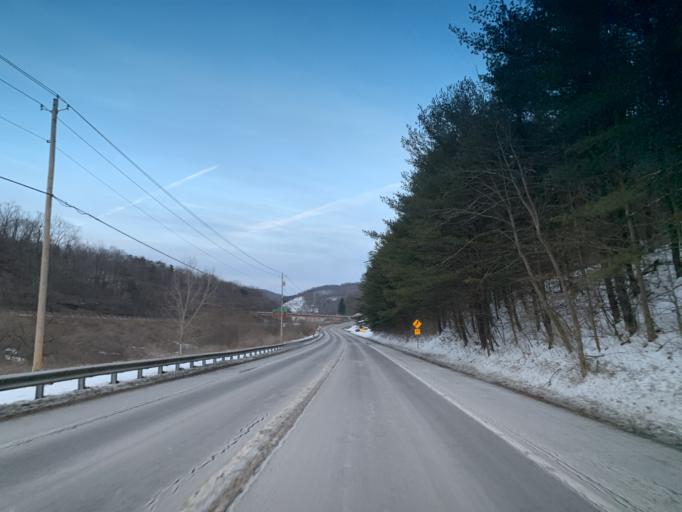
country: US
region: Maryland
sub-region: Allegany County
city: Cumberland
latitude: 39.6808
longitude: -78.6731
